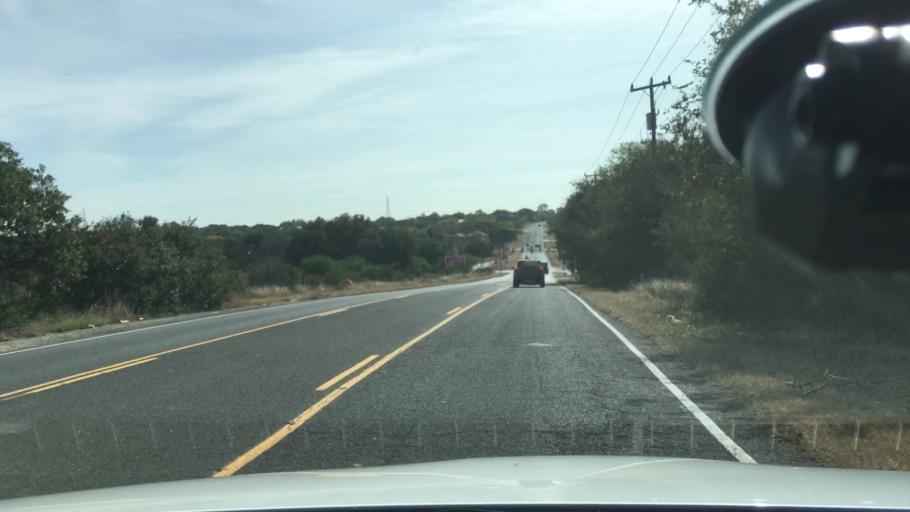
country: US
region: Texas
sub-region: Bexar County
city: Hollywood Park
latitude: 29.5814
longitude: -98.4213
